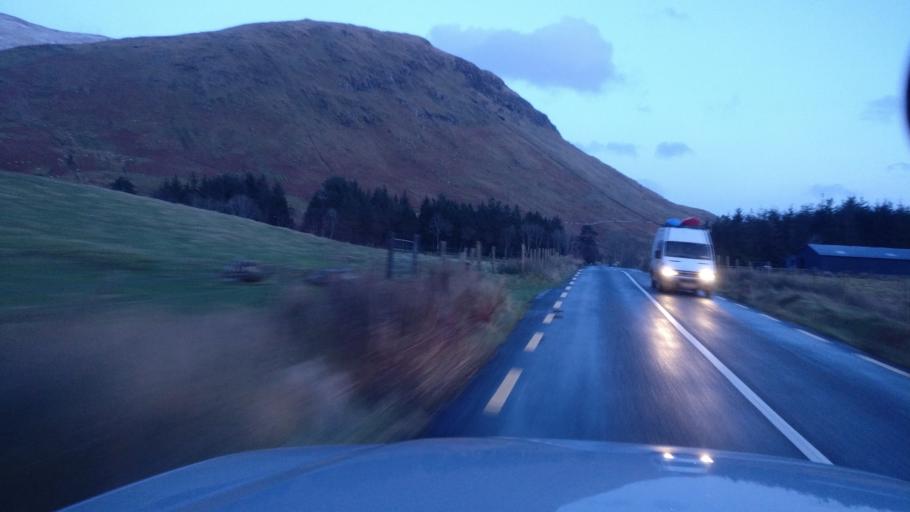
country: IE
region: Connaught
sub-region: Maigh Eo
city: Westport
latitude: 53.5486
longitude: -9.6290
